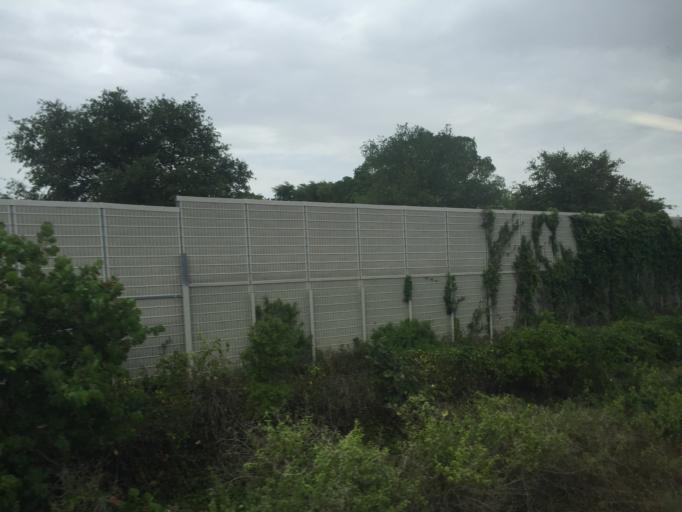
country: US
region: Florida
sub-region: Broward County
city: Dania Beach
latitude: 26.0454
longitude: -80.1680
